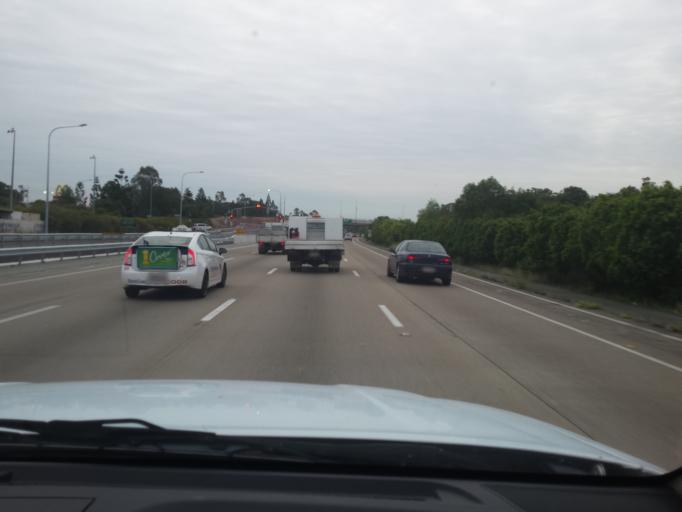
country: AU
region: Queensland
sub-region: Gold Coast
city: Oxenford
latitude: -27.8609
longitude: 153.3101
